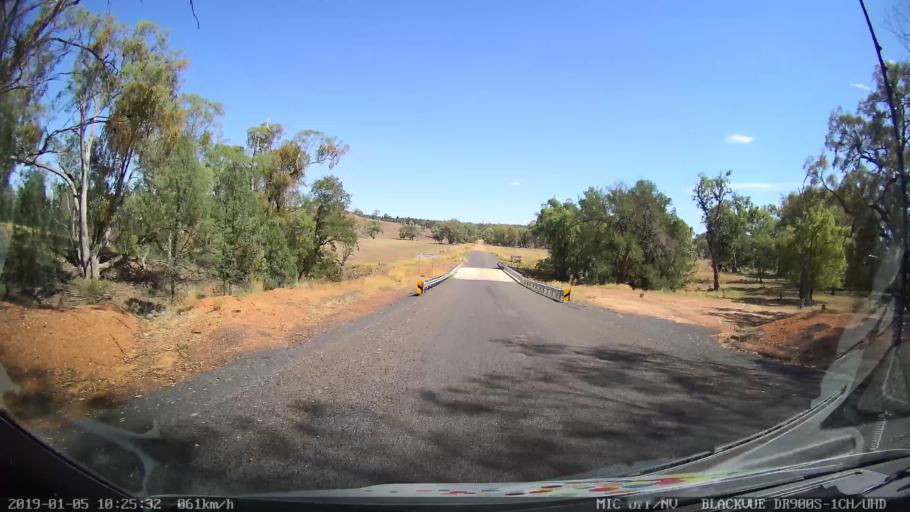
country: AU
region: New South Wales
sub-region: Gilgandra
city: Gilgandra
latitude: -31.5606
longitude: 148.9590
